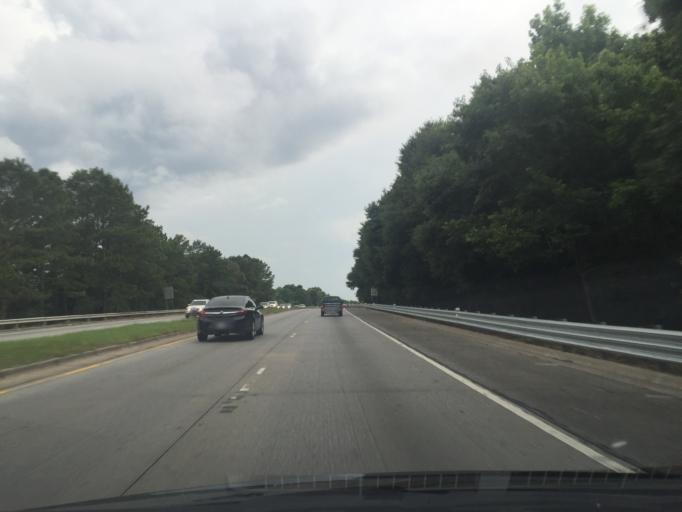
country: US
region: Georgia
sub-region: Chatham County
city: Savannah
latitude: 32.0347
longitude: -81.1322
